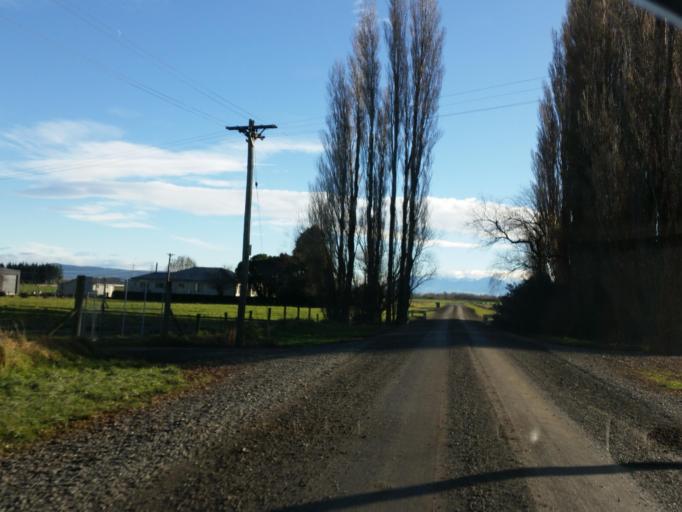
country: NZ
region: Southland
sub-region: Southland District
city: Winton
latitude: -46.0895
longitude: 168.0949
